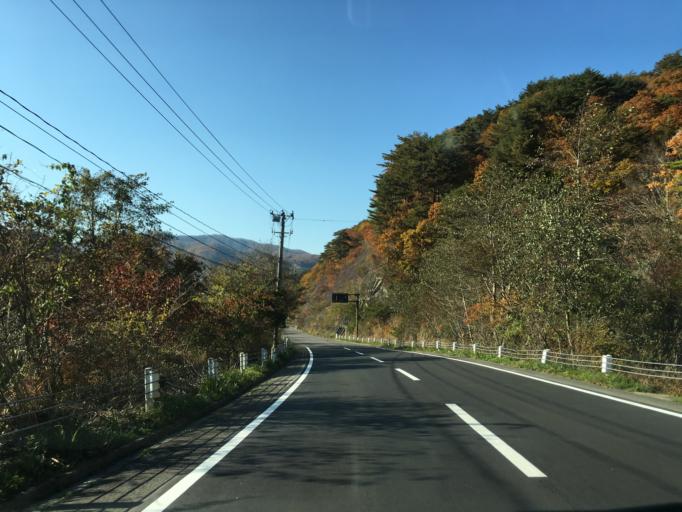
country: JP
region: Fukushima
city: Inawashiro
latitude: 37.2736
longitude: 140.0744
